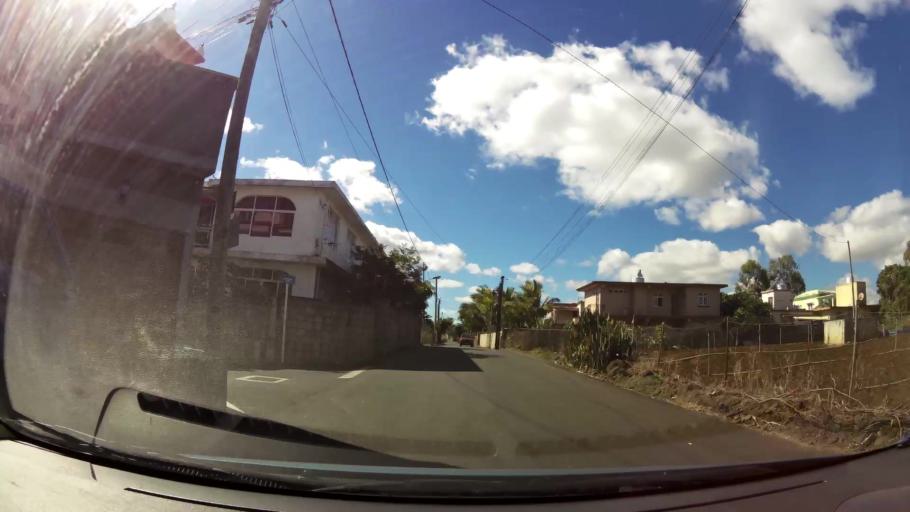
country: MU
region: Plaines Wilhems
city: Vacoas
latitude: -20.2928
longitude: 57.4737
